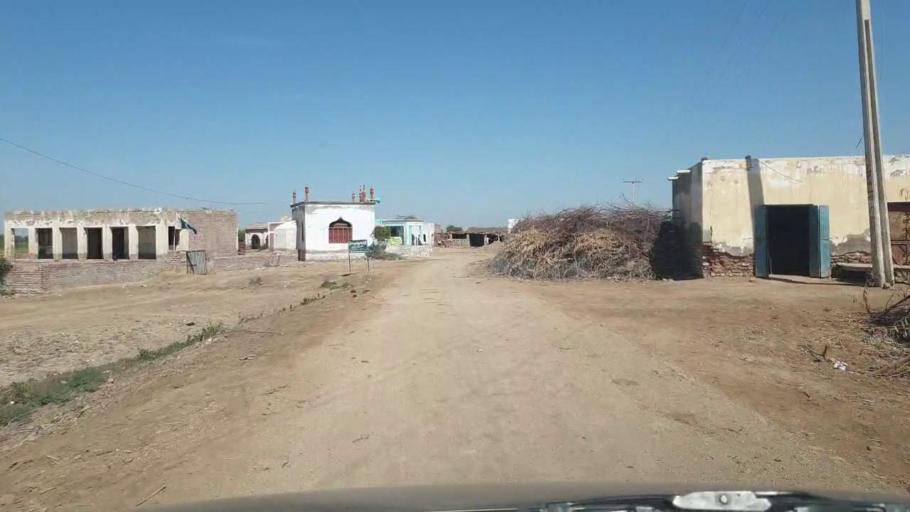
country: PK
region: Sindh
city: Umarkot
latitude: 25.4006
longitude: 69.6320
